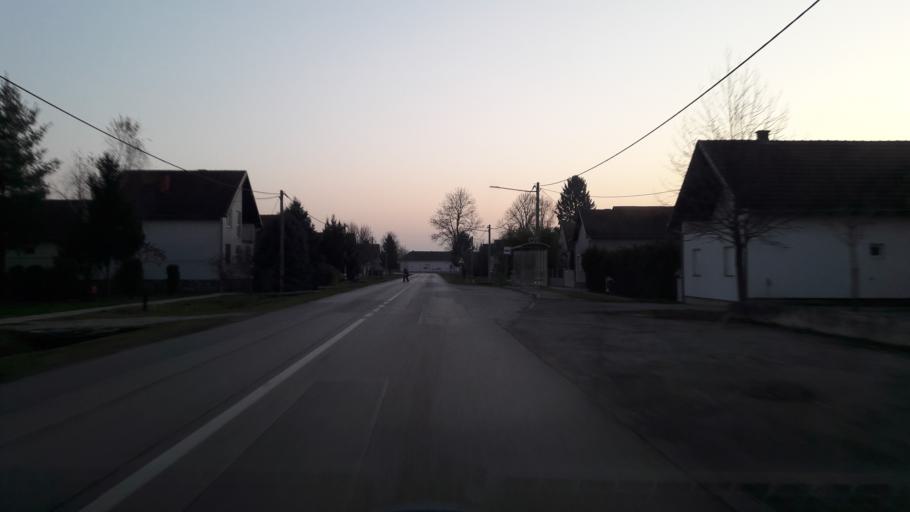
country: HR
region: Vukovarsko-Srijemska
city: Nijemci
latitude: 45.1812
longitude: 19.0122
